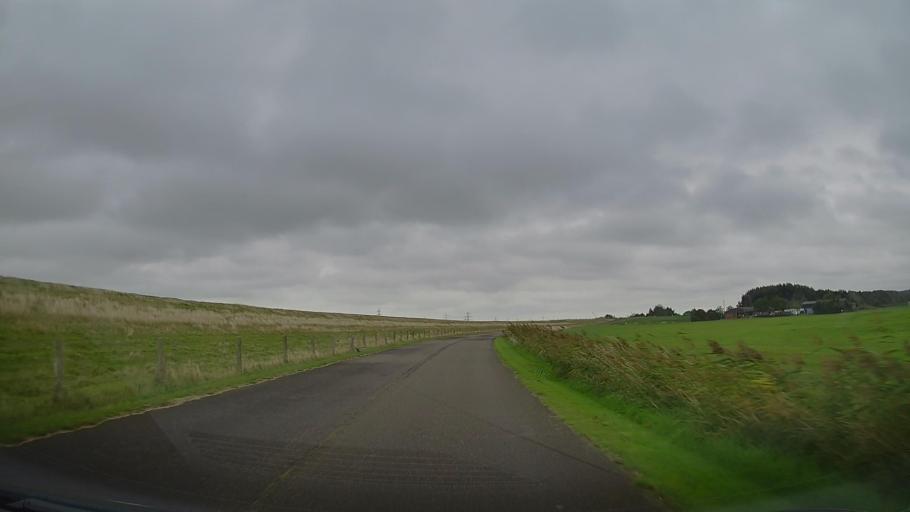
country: DE
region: Schleswig-Holstein
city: Elpersbuttel
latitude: 54.0726
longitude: 9.0099
